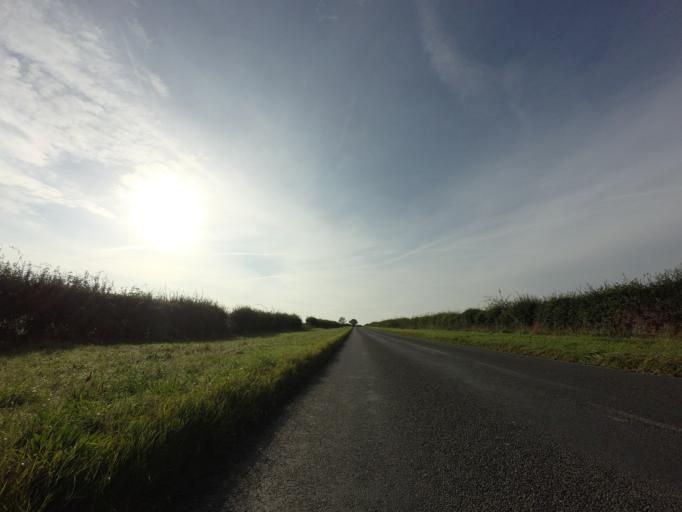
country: GB
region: England
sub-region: Cambridgeshire
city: Harston
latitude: 52.1355
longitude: 0.0997
